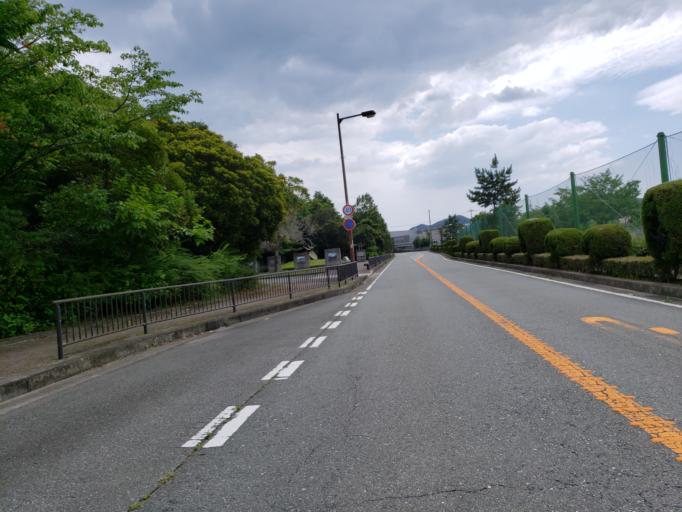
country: JP
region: Hyogo
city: Aioi
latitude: 34.7811
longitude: 134.4738
